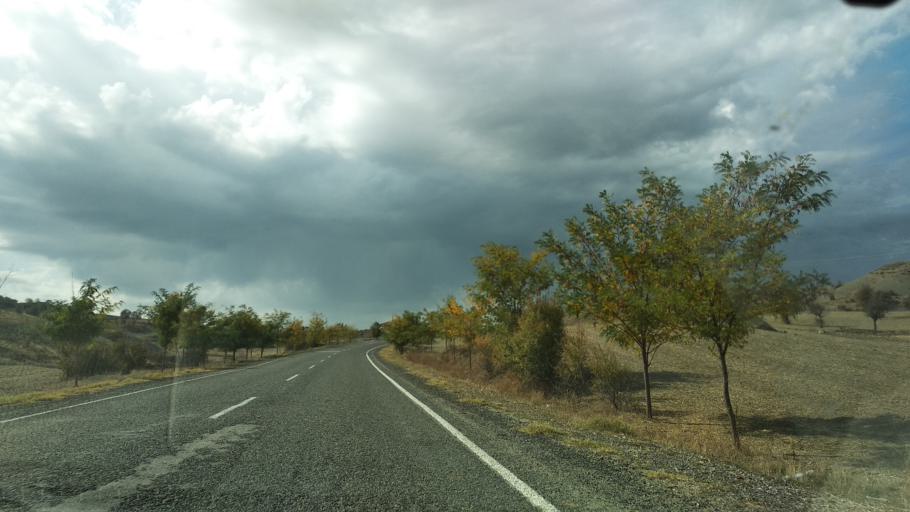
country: TR
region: Bolu
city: Seben
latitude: 40.3796
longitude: 31.5231
